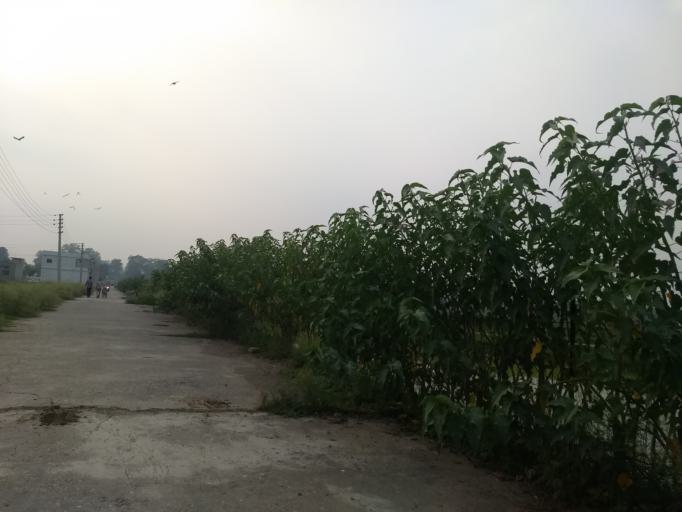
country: IN
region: Uttarakhand
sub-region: Dehradun
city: Raiwala
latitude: 30.0372
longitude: 78.2177
